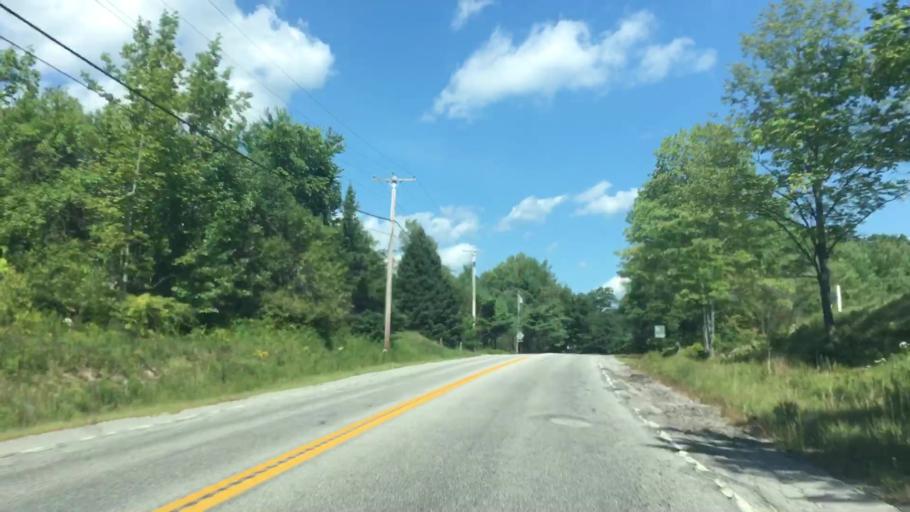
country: US
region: Maine
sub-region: Cumberland County
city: New Gloucester
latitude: 43.9189
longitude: -70.3164
